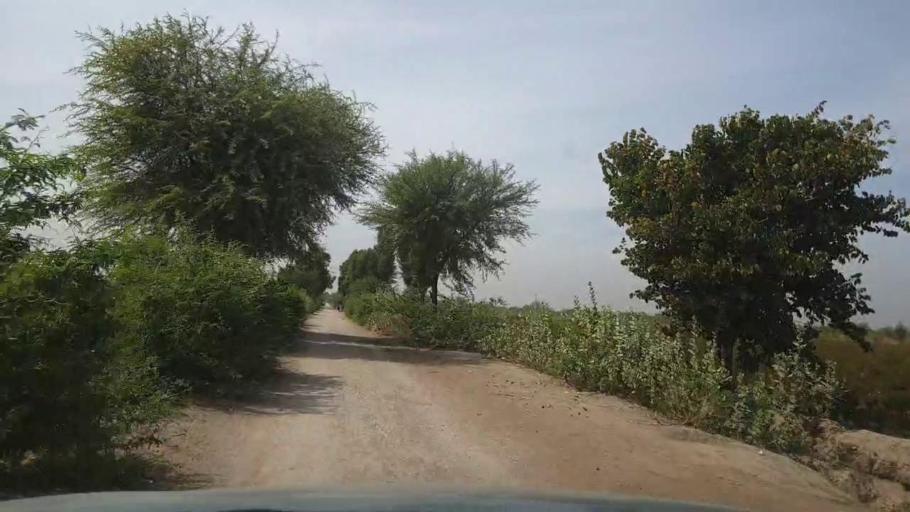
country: PK
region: Sindh
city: Nabisar
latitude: 25.0723
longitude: 69.5981
